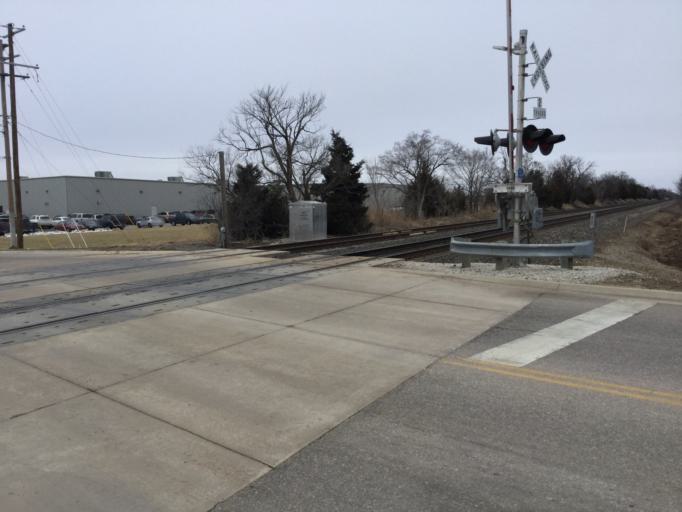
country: US
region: Kansas
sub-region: Sedgwick County
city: Derby
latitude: 37.5480
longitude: -97.2725
